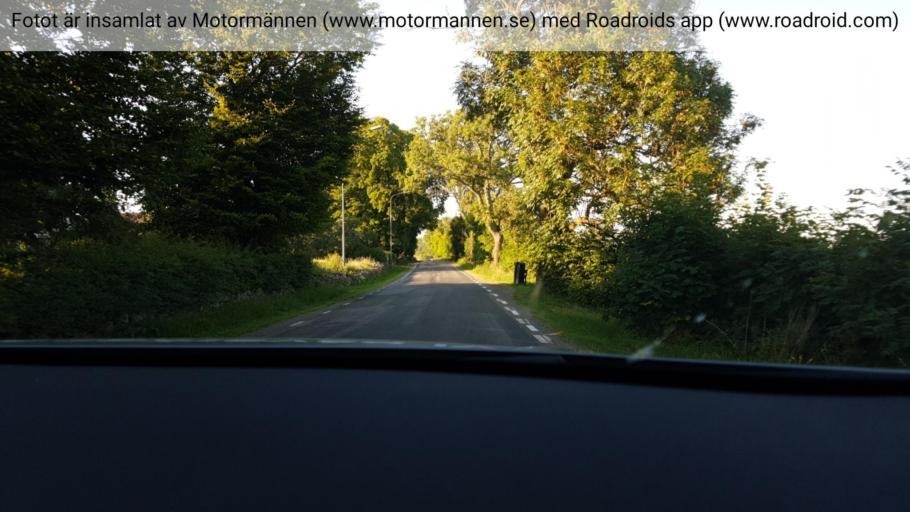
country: SE
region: Vaestra Goetaland
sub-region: Skovde Kommun
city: Skultorp
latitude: 58.2815
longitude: 13.7932
